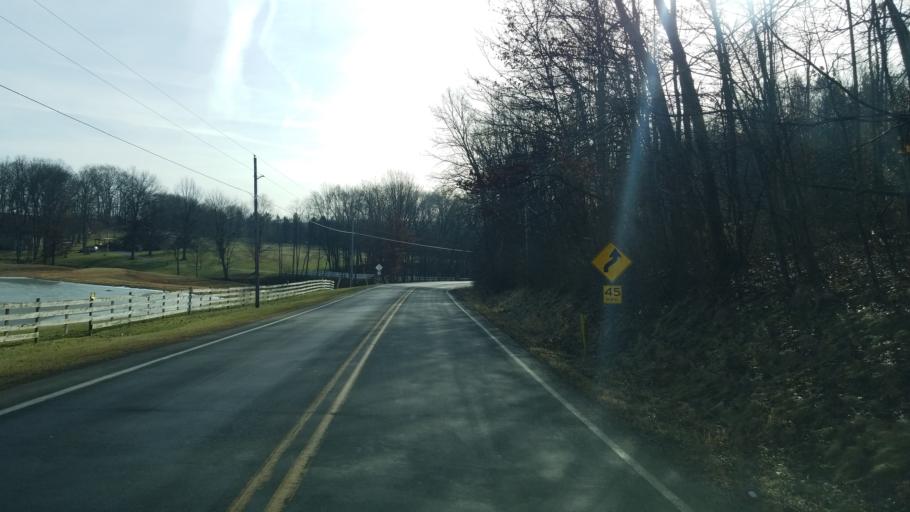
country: US
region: Pennsylvania
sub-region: Indiana County
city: Chevy Chase Heights
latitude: 40.7478
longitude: -79.1090
